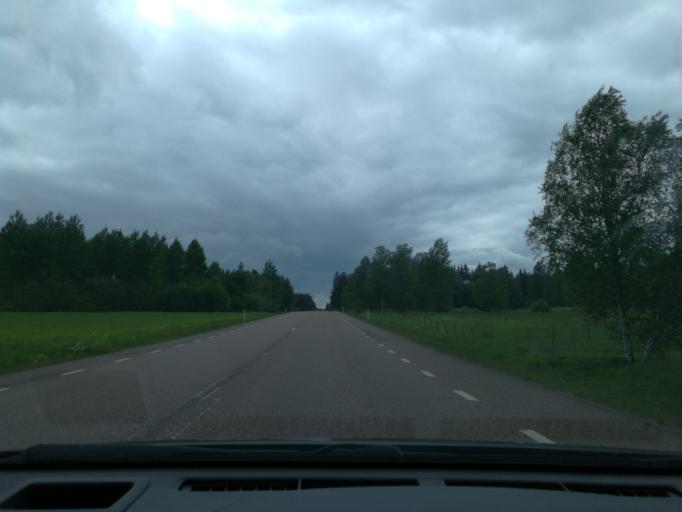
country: SE
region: Dalarna
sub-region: Smedjebackens Kommun
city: Smedjebacken
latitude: 60.1405
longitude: 15.3642
